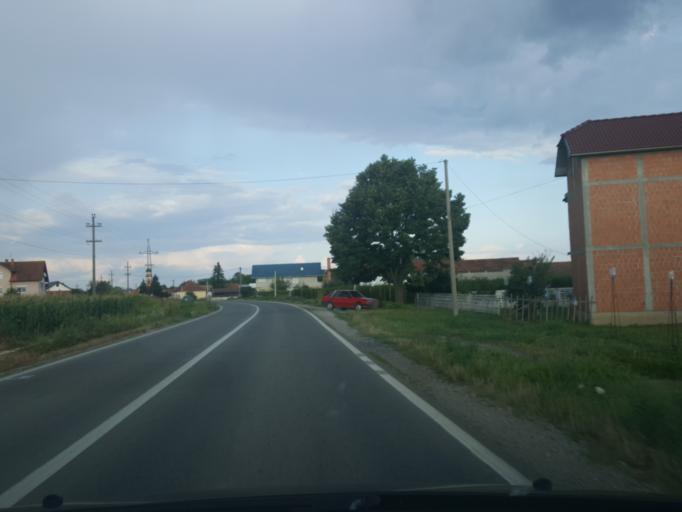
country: RS
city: Ribari
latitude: 44.7065
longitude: 19.4122
